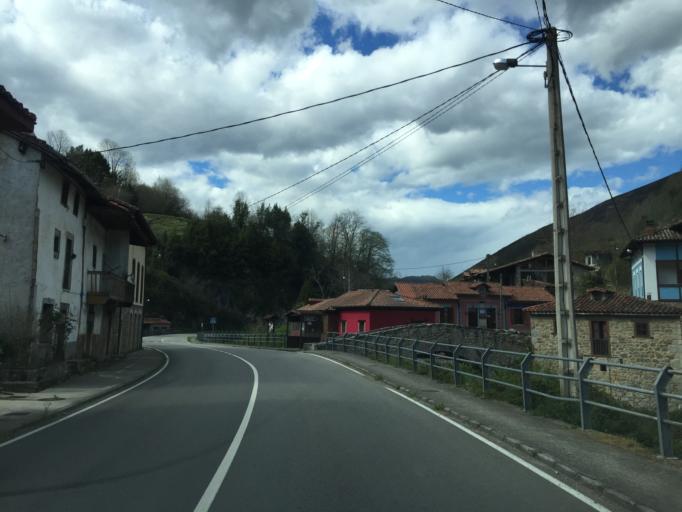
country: ES
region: Asturias
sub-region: Province of Asturias
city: Cangas de Onis
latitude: 43.3243
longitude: -5.0781
